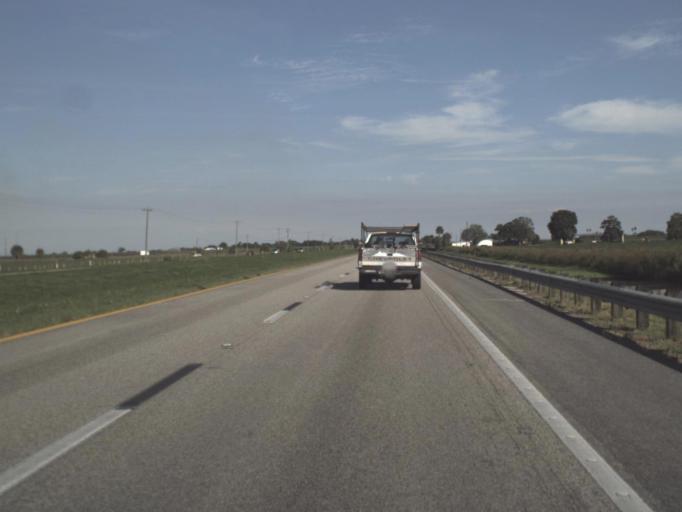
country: US
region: Florida
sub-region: Hendry County
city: Harlem
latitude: 26.7539
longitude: -81.0123
